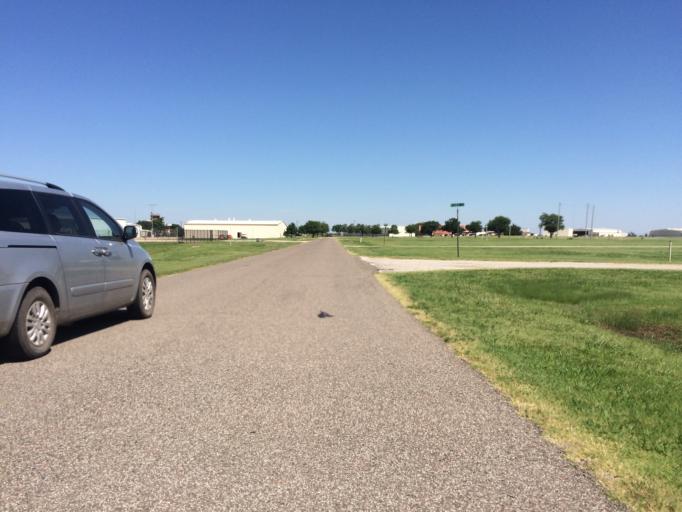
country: US
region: Oklahoma
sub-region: Cleveland County
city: Norman
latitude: 35.2384
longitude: -97.4642
